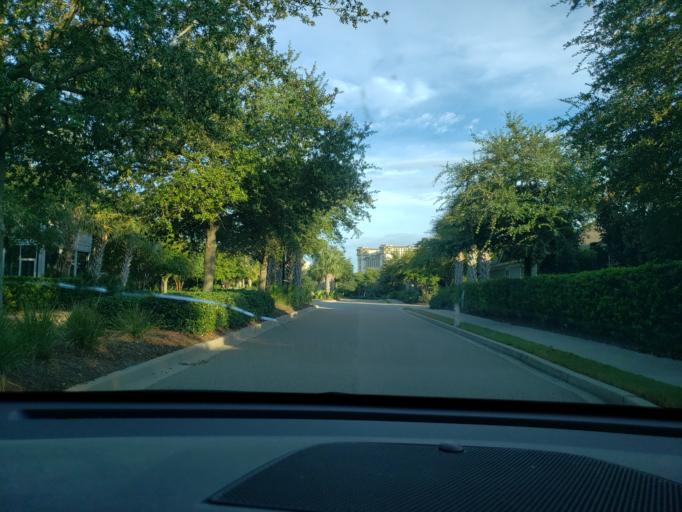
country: US
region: South Carolina
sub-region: Horry County
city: North Myrtle Beach
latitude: 33.7948
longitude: -78.7407
